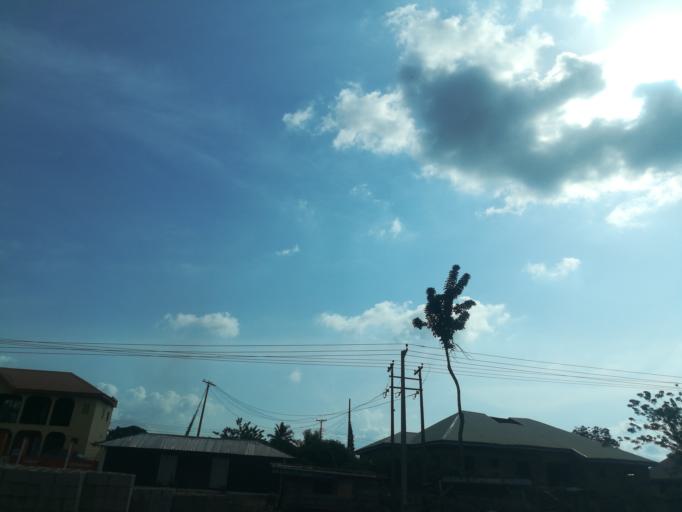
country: NG
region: Oyo
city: Ido
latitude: 7.3988
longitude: 3.8056
